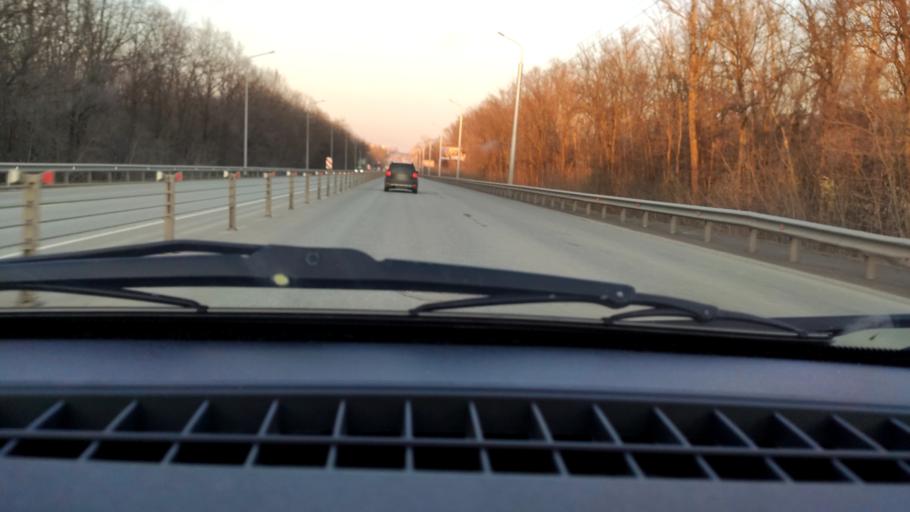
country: RU
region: Bashkortostan
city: Ufa
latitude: 54.7018
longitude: 55.9224
